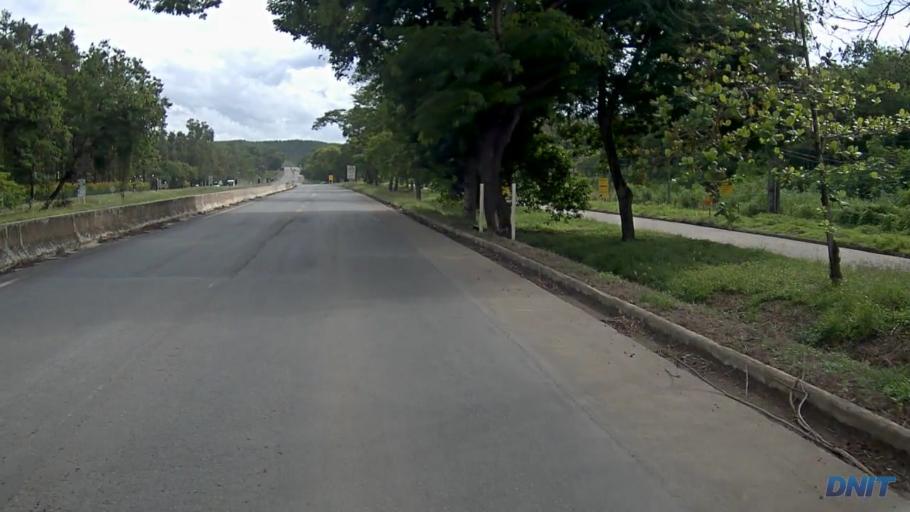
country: BR
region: Minas Gerais
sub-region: Ipaba
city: Ipaba
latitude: -19.3125
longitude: -42.3959
